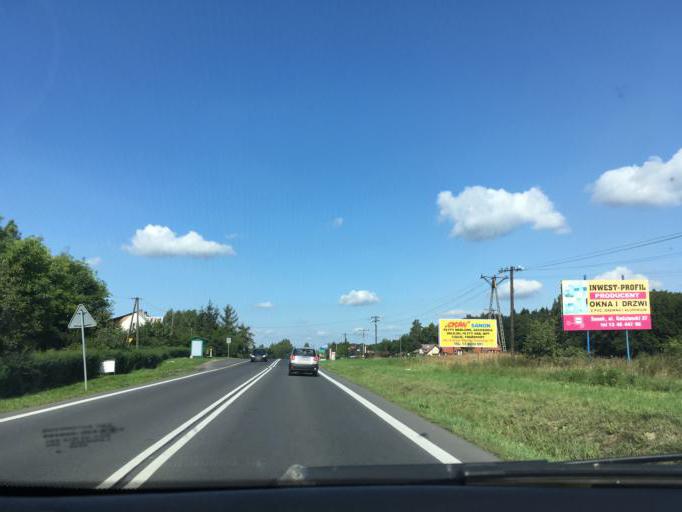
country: PL
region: Subcarpathian Voivodeship
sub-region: Powiat sanocki
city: Zagorz
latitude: 49.5250
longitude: 22.2458
